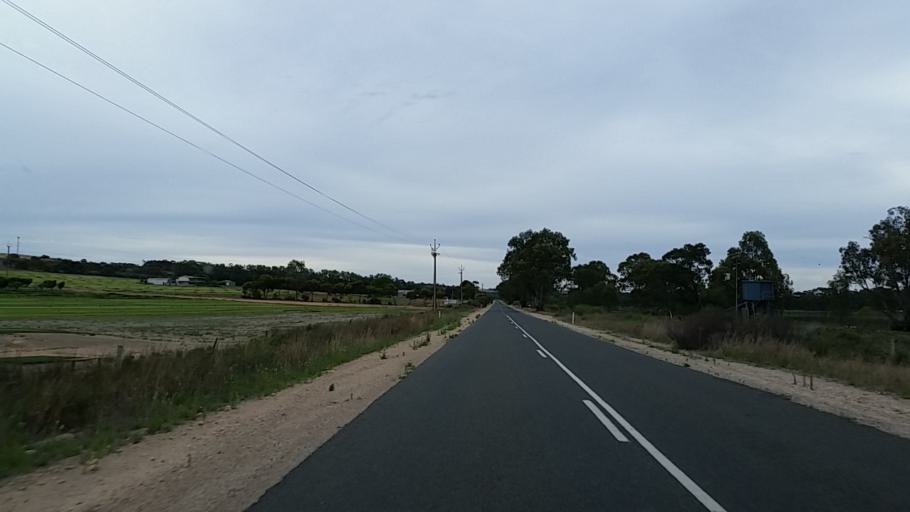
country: AU
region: South Australia
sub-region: Mid Murray
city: Mannum
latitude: -34.7604
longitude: 139.5665
